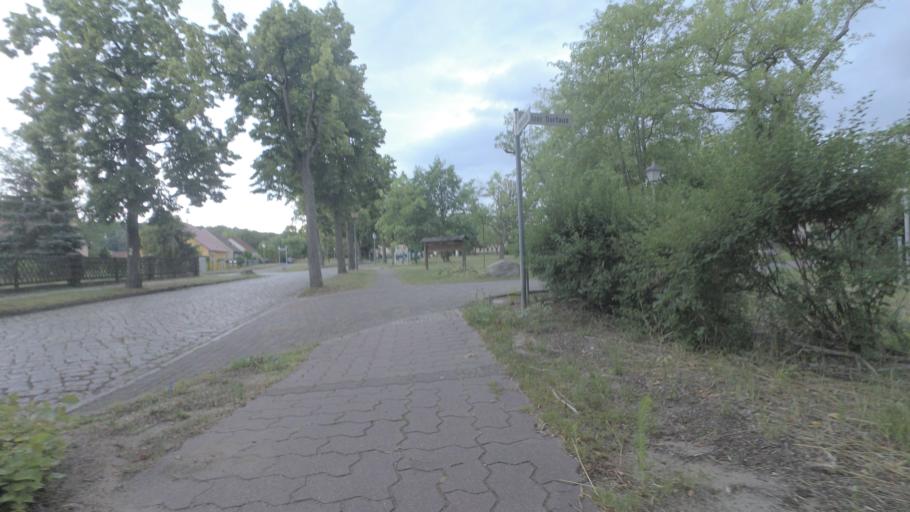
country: DE
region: Brandenburg
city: Bestensee
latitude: 52.2258
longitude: 13.6560
